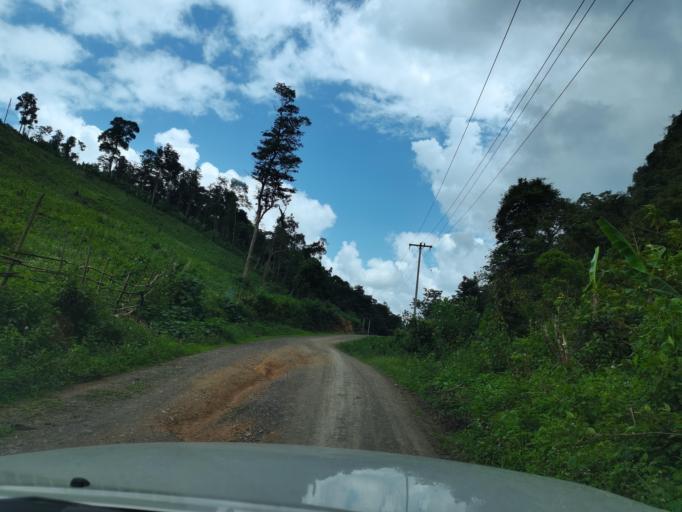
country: LA
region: Loungnamtha
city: Muang Long
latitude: 20.7785
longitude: 101.0166
